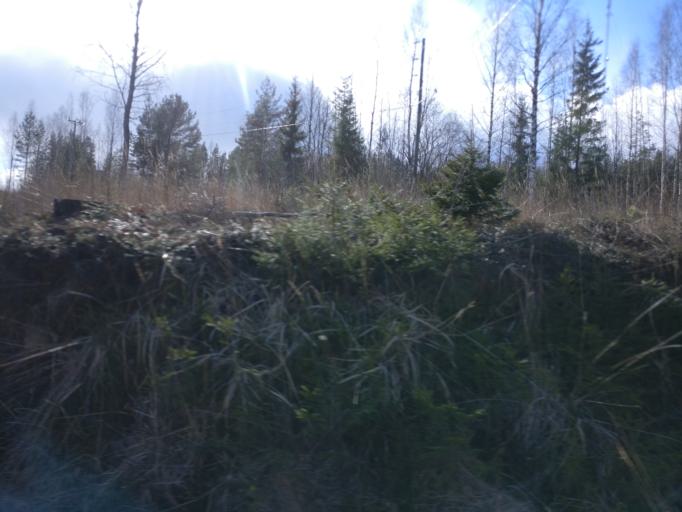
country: FI
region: Varsinais-Suomi
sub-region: Salo
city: Suomusjaervi
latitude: 60.3054
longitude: 23.6475
